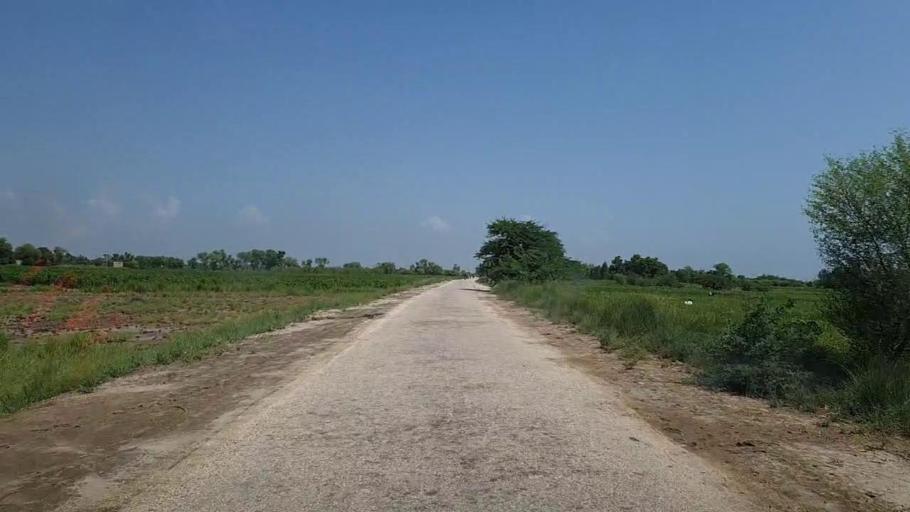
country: PK
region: Sindh
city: Bhiria
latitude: 26.8963
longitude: 68.2200
